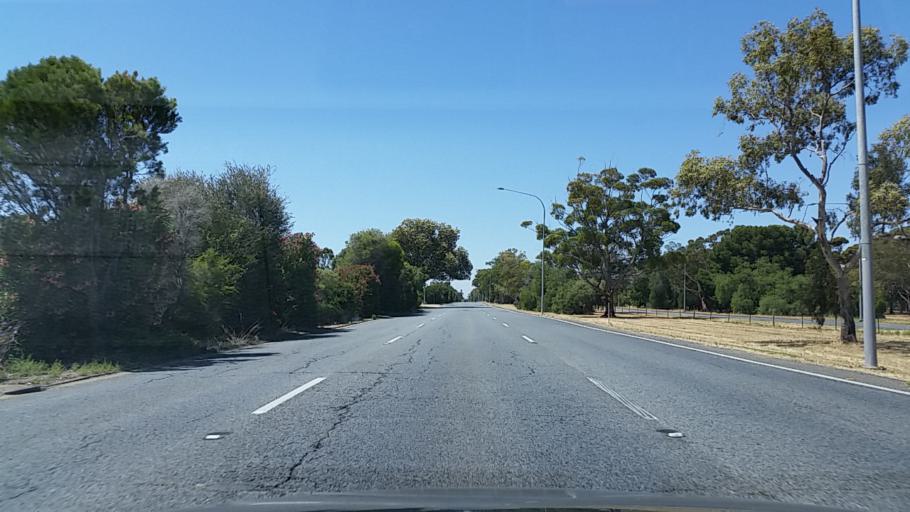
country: AU
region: South Australia
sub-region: Salisbury
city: Elizabeth
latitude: -34.7046
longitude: 138.6800
